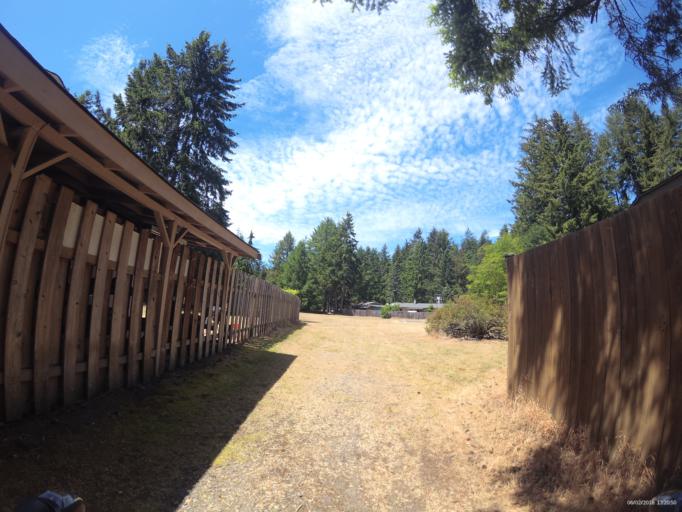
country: US
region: Washington
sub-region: Pierce County
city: University Place
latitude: 47.2092
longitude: -122.5606
